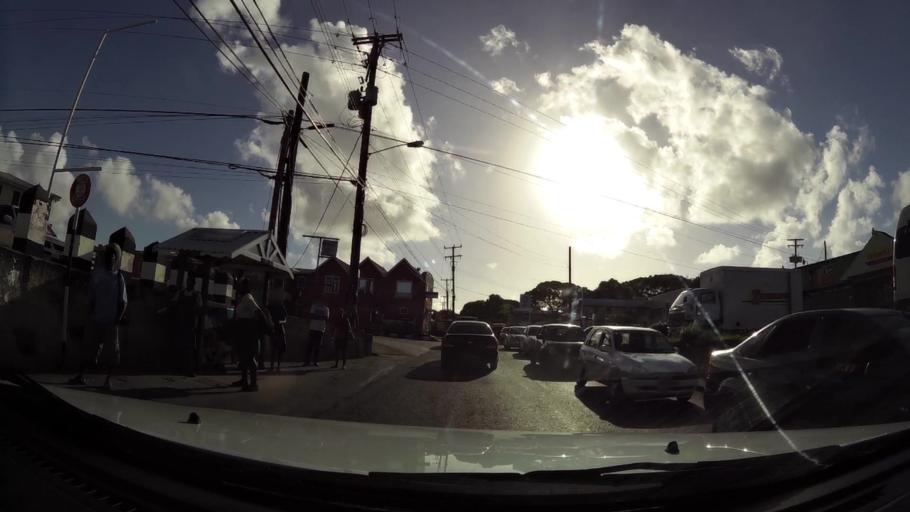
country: BB
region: Saint Michael
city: Bridgetown
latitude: 13.0933
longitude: -59.5930
